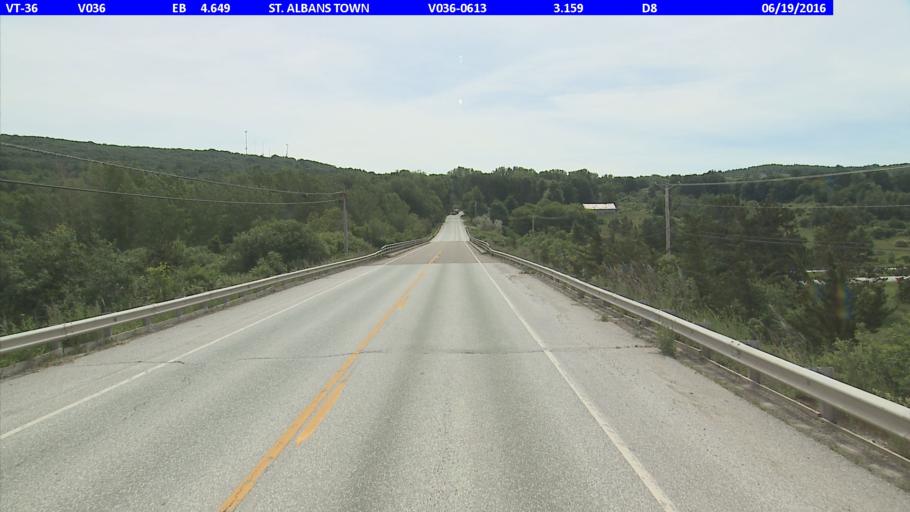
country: US
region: Vermont
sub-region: Franklin County
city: Saint Albans
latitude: 44.8041
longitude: -73.0661
